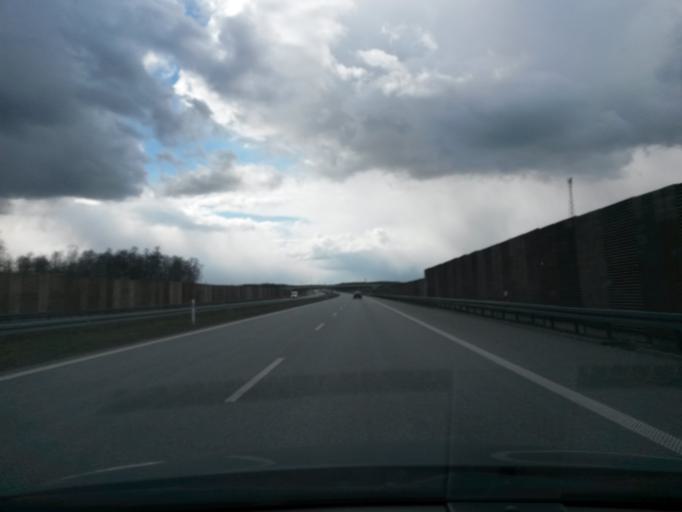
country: PL
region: Greater Poland Voivodeship
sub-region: Powiat koninski
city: Krzymow
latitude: 52.1425
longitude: 18.3861
